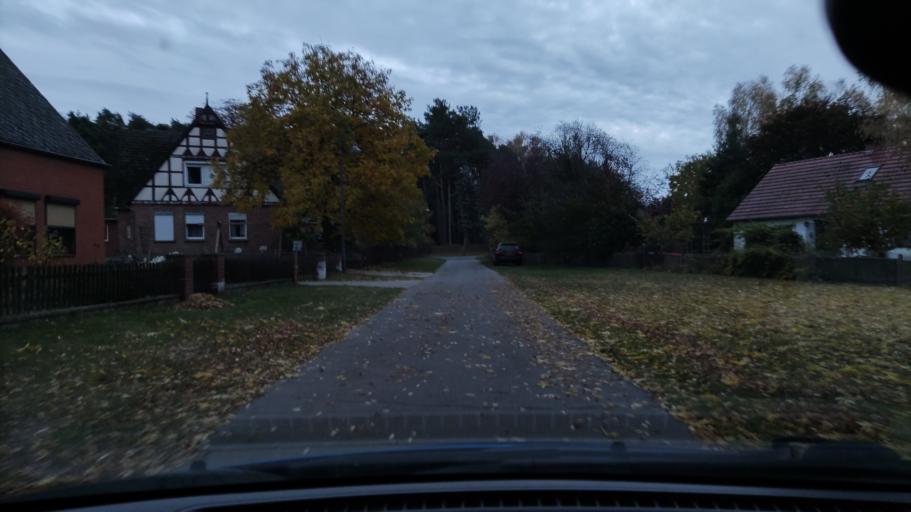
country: DE
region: Lower Saxony
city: Prezelle
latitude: 52.9633
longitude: 11.4052
